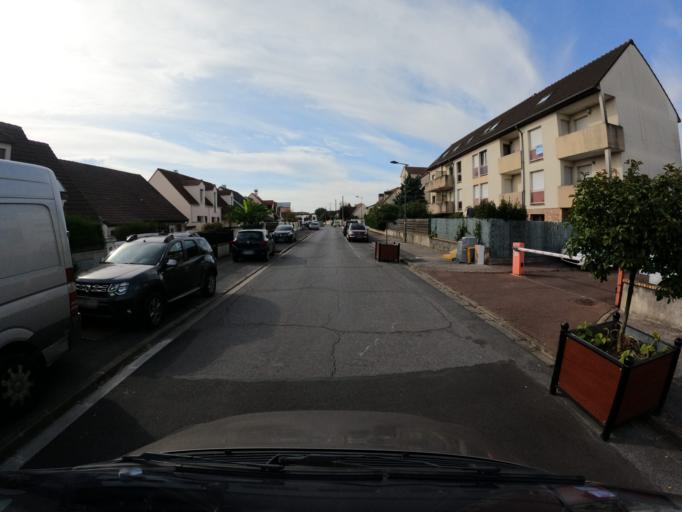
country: FR
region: Ile-de-France
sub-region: Departement de Seine-et-Marne
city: Pontault-Combault
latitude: 48.7860
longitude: 2.6125
